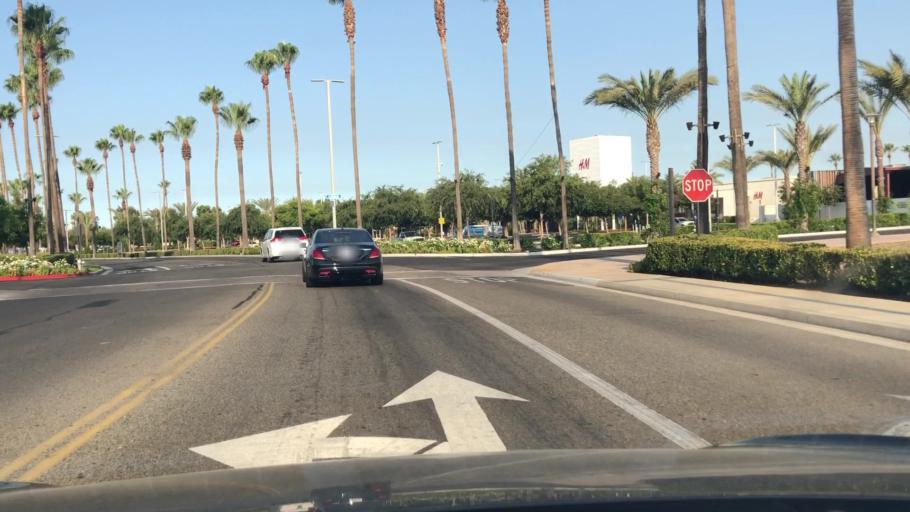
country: US
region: California
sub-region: Fresno County
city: Clovis
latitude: 36.8483
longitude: -119.7868
